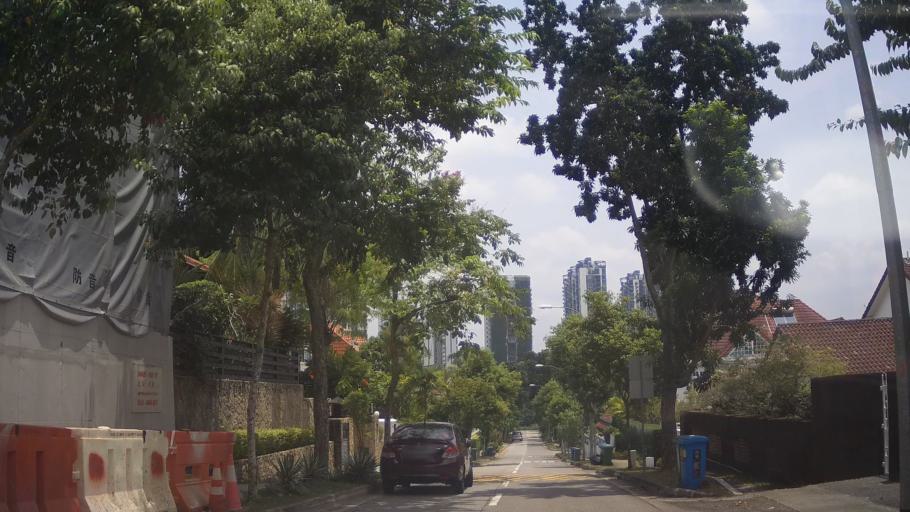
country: MY
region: Johor
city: Johor Bahru
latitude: 1.3703
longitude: 103.7711
